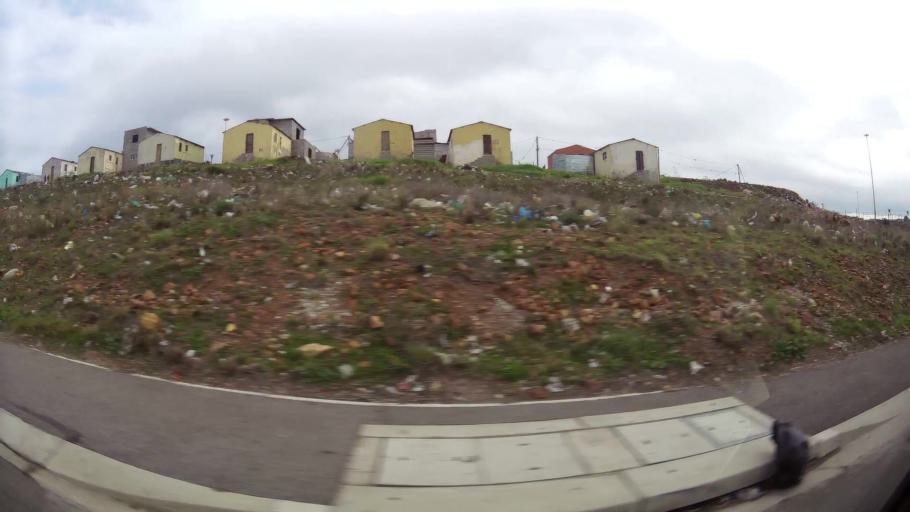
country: ZA
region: Eastern Cape
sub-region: Nelson Mandela Bay Metropolitan Municipality
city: Port Elizabeth
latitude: -33.9128
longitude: 25.5379
